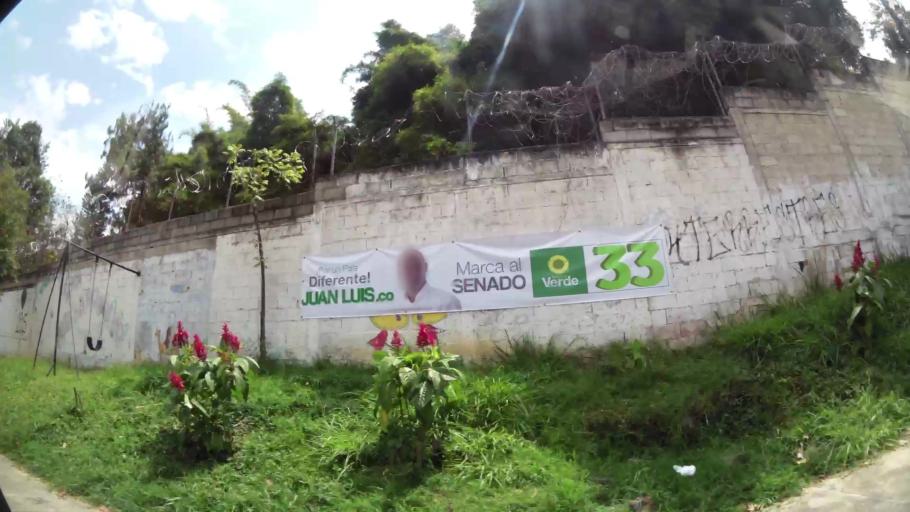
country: CO
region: Antioquia
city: Medellin
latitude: 6.2500
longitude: -75.6189
